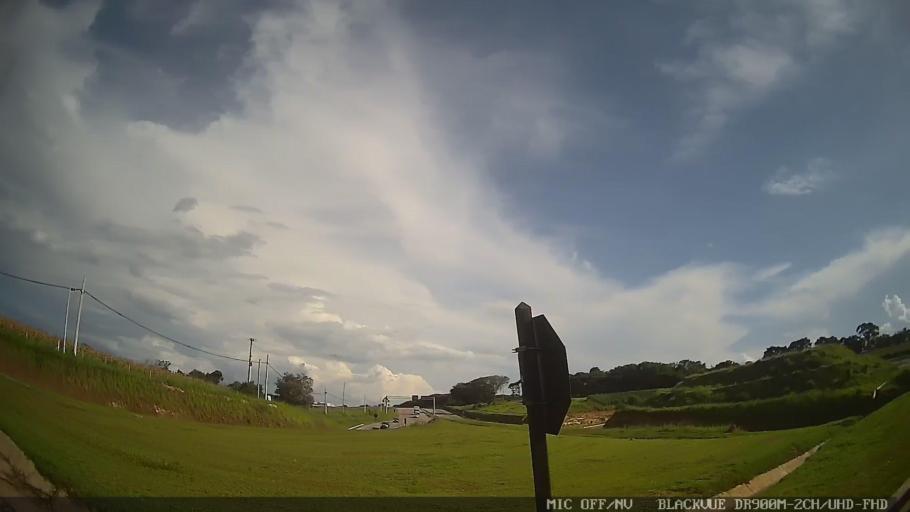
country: BR
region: Sao Paulo
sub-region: Tiete
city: Tiete
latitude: -23.1201
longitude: -47.7004
